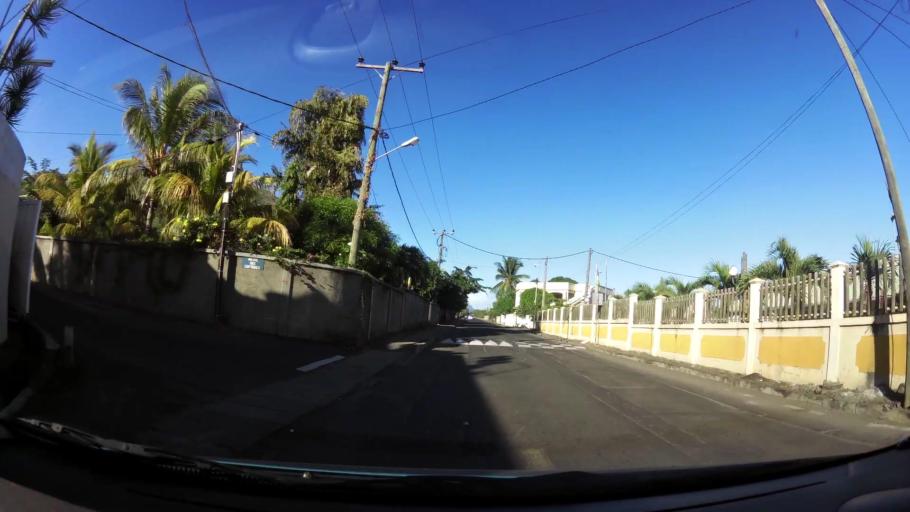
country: MU
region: Black River
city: Tamarin
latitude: -20.3330
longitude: 57.3721
